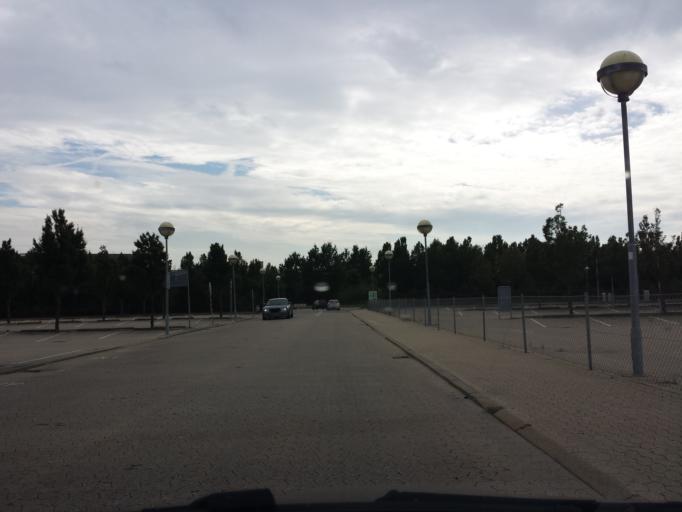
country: DK
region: Capital Region
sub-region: Hoje-Taastrup Kommune
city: Taastrup
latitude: 55.6472
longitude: 12.2683
